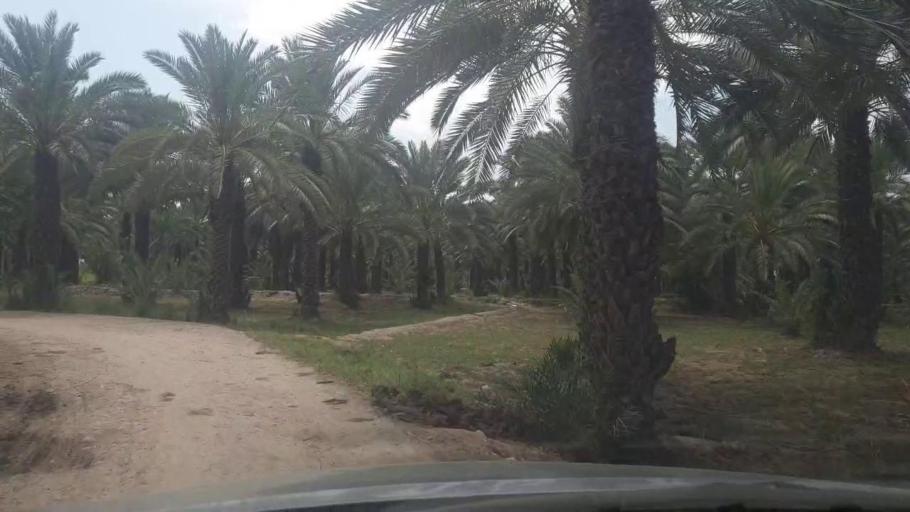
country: PK
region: Sindh
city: Kot Diji
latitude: 27.3988
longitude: 68.7573
